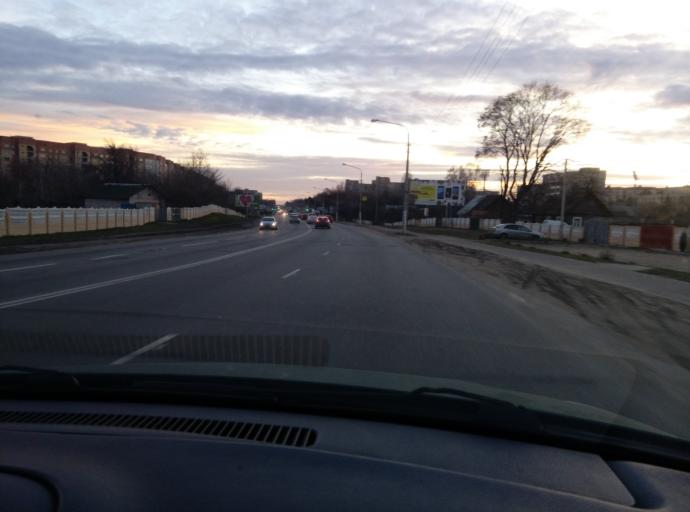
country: BY
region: Minsk
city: Horad Barysaw
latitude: 54.2258
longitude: 28.4949
